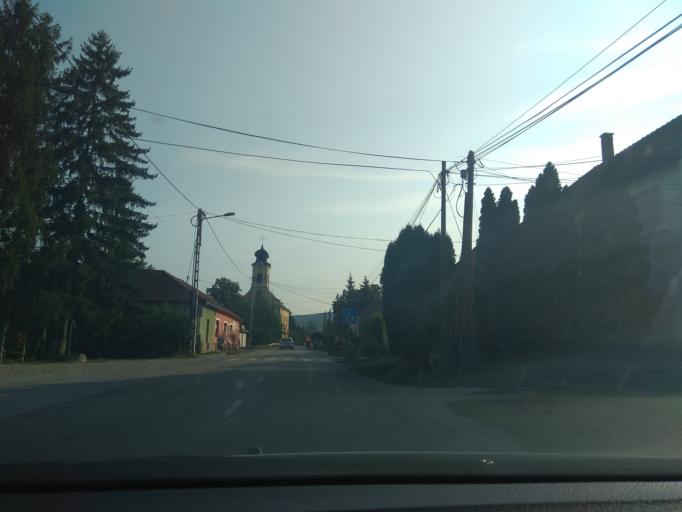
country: HU
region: Heves
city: Felsotarkany
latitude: 47.9709
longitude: 20.4123
